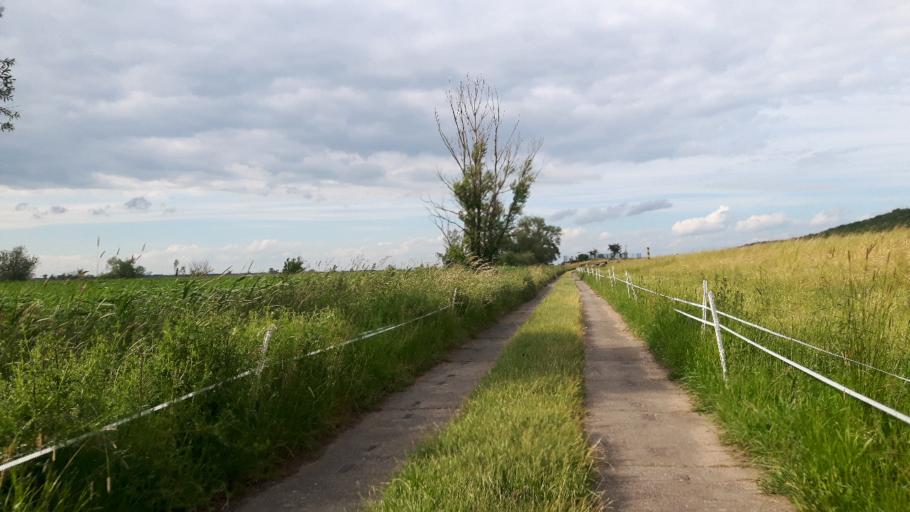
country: PL
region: West Pomeranian Voivodeship
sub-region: Powiat gryfinski
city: Widuchowa
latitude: 53.0895
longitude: 14.3670
